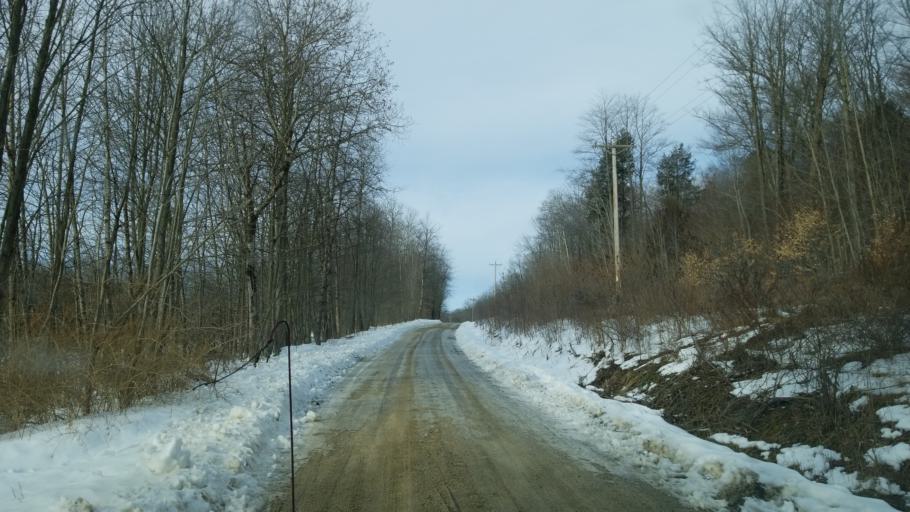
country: US
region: Pennsylvania
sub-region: Tioga County
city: Westfield
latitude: 41.9601
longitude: -77.7199
